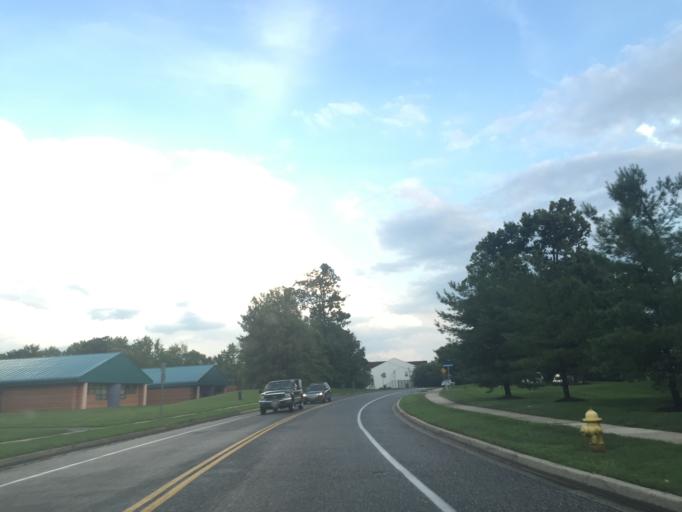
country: US
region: Maryland
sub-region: Harford County
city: Riverside
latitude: 39.4760
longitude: -76.2490
